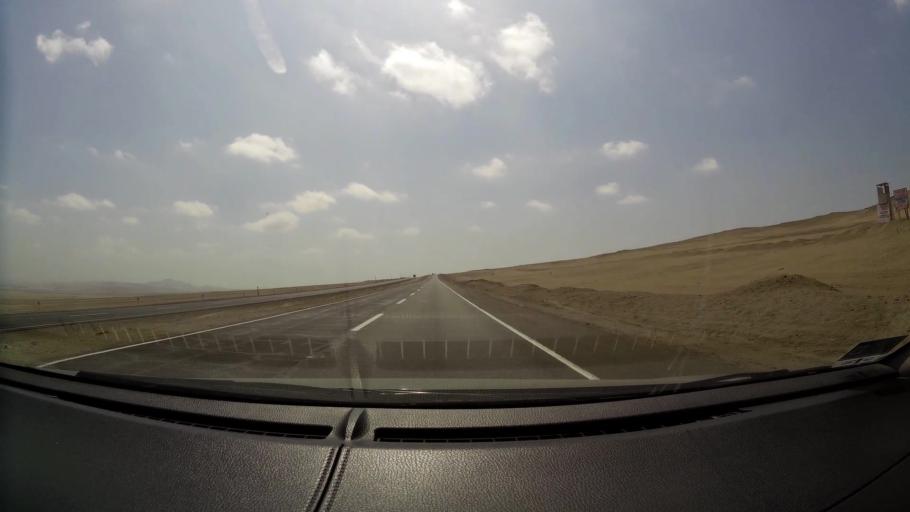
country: PE
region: Lima
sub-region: Huaura
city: Huacho
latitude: -11.2752
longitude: -77.5108
